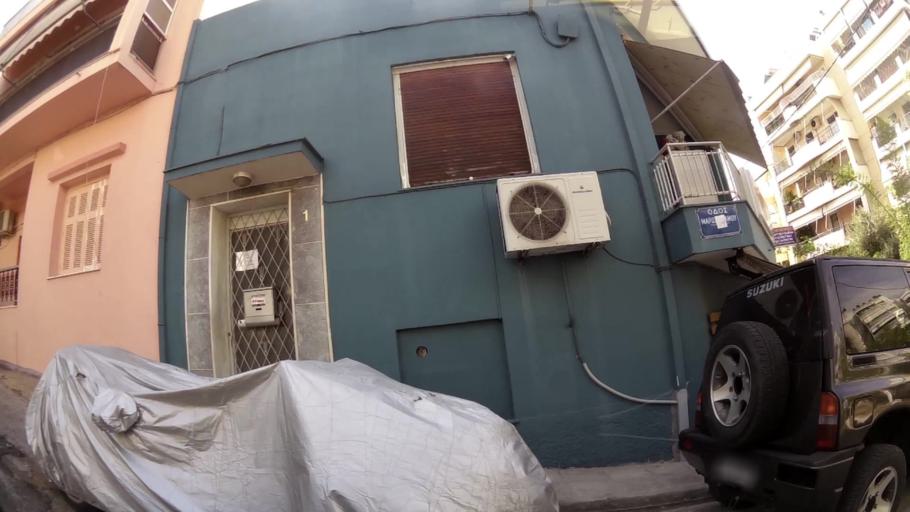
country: GR
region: Attica
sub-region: Nomarchia Athinas
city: Athens
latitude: 37.9649
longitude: 23.7102
